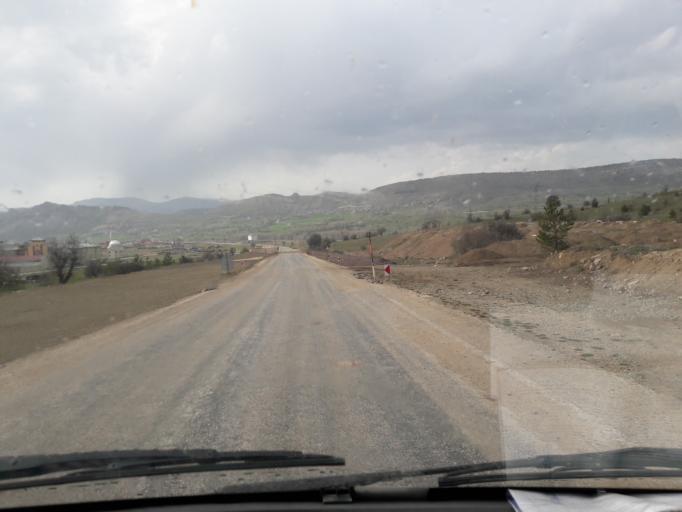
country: TR
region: Giresun
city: Alucra
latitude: 40.3209
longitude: 38.7736
